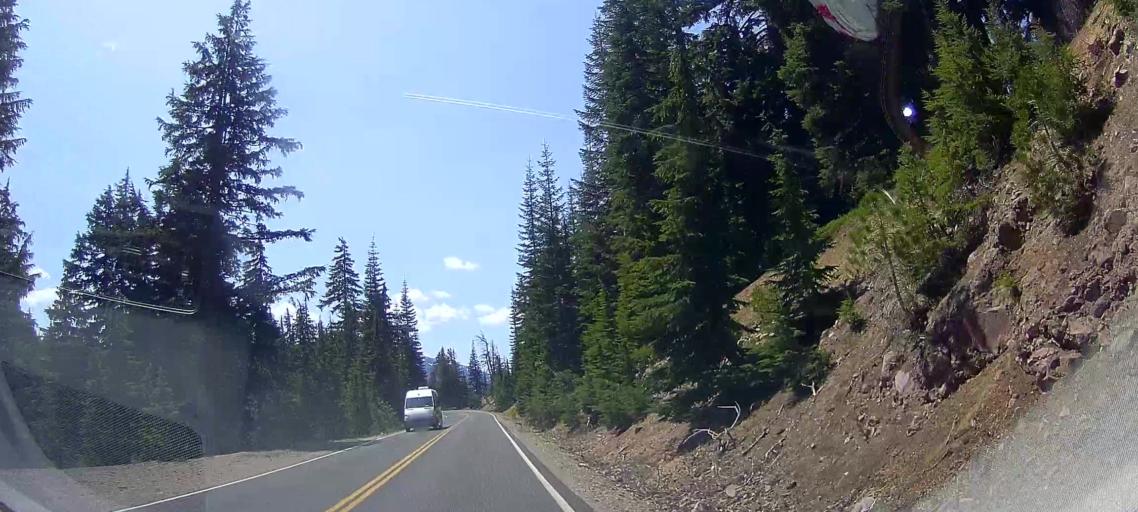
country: US
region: Oregon
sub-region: Jackson County
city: Shady Cove
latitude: 42.9794
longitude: -122.1070
